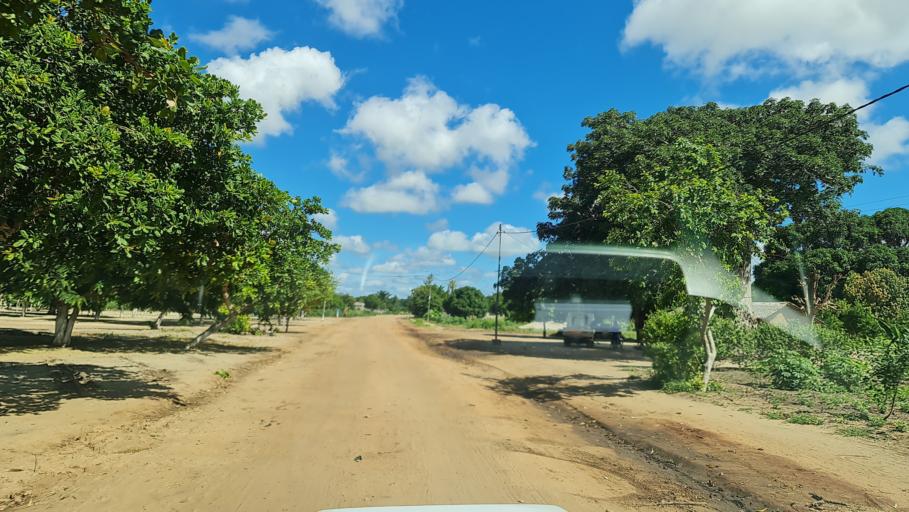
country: MZ
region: Nampula
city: Ilha de Mocambique
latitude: -15.5558
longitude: 40.4111
